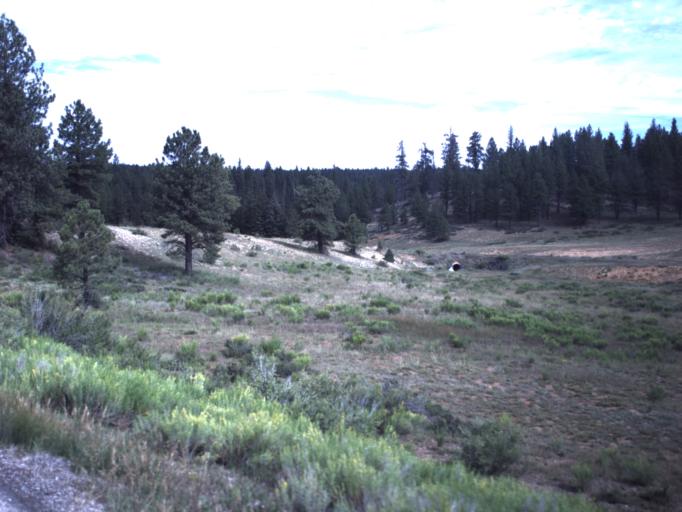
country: US
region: Utah
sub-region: Garfield County
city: Panguitch
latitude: 37.4968
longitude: -112.5851
